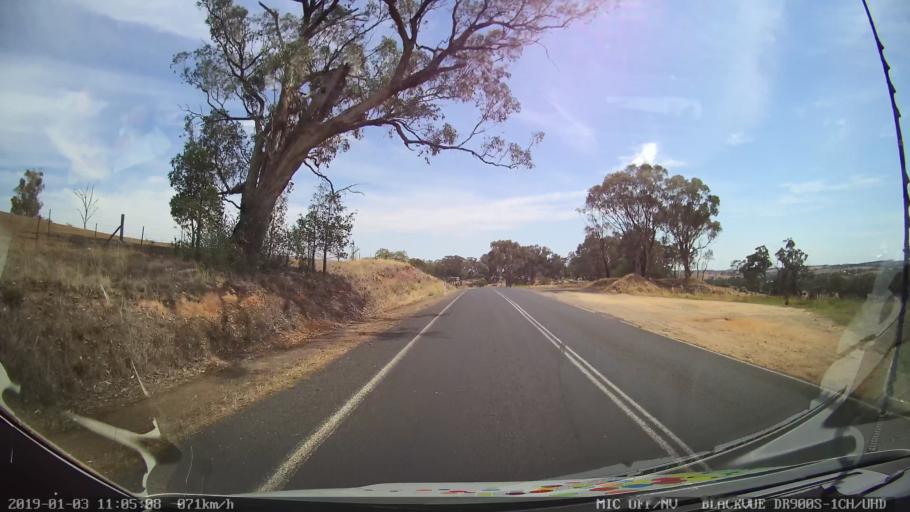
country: AU
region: New South Wales
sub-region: Young
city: Young
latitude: -34.2748
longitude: 148.2863
